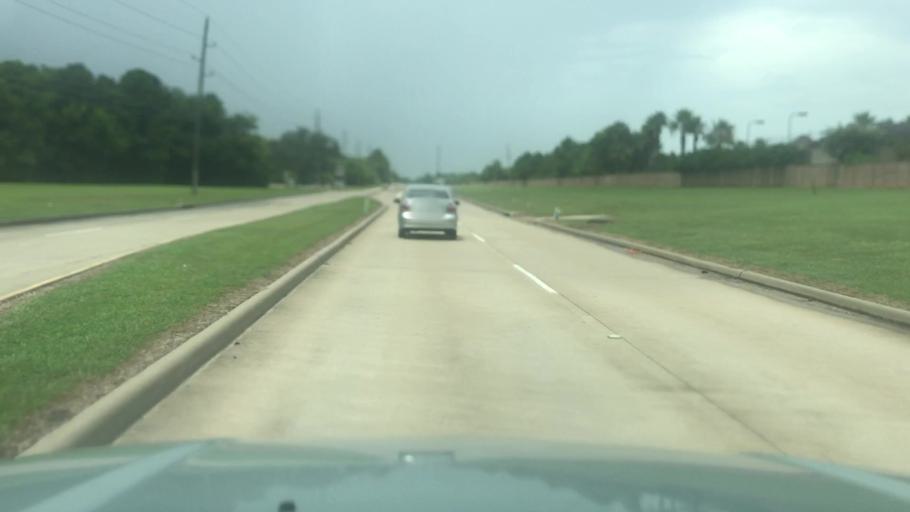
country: US
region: Texas
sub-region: Harris County
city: Katy
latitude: 29.7539
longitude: -95.8028
